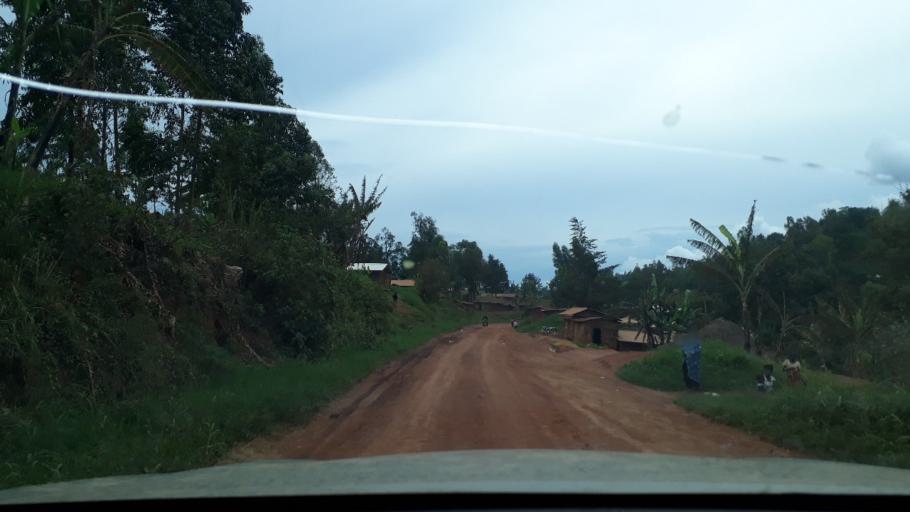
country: CD
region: Eastern Province
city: Bunia
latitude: 1.7430
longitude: 30.3480
